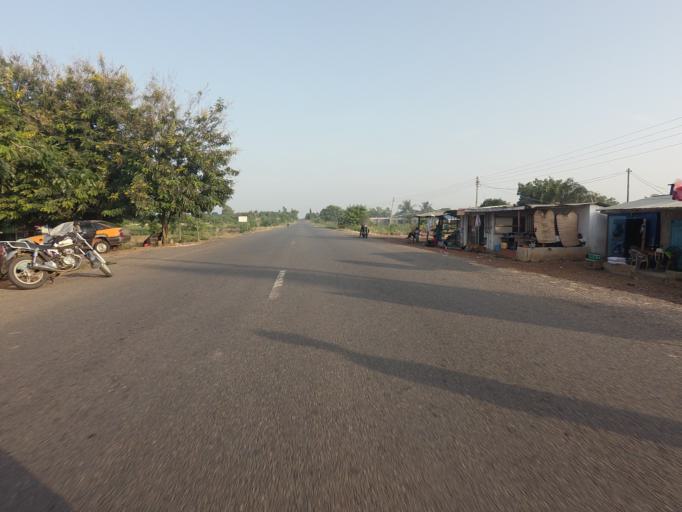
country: GH
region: Volta
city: Anloga
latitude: 6.0187
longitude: 0.6653
